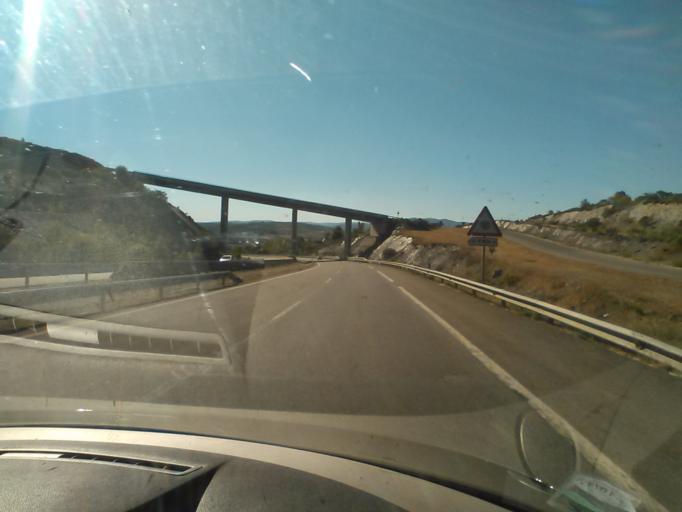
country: ES
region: Castille and Leon
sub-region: Provincia de Zamora
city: Pias
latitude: 42.0577
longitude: -7.1151
